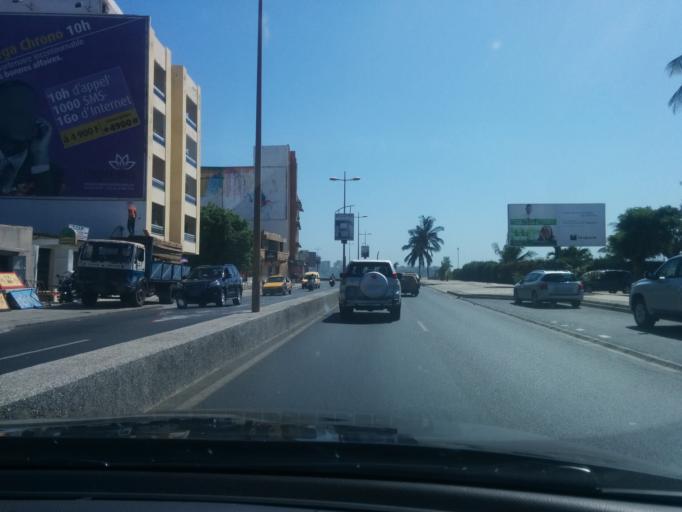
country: SN
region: Dakar
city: Dakar
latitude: 14.6754
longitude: -17.4534
